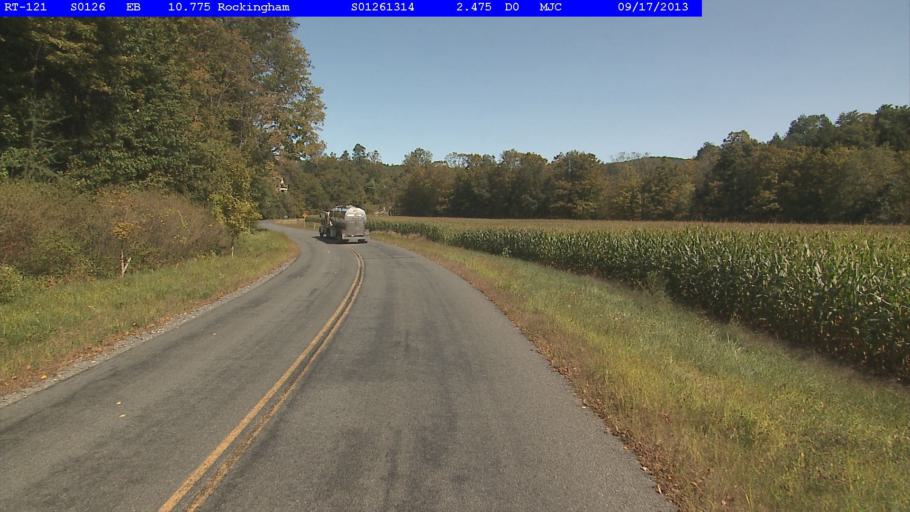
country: US
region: Vermont
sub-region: Windham County
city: Rockingham
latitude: 43.1353
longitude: -72.5169
